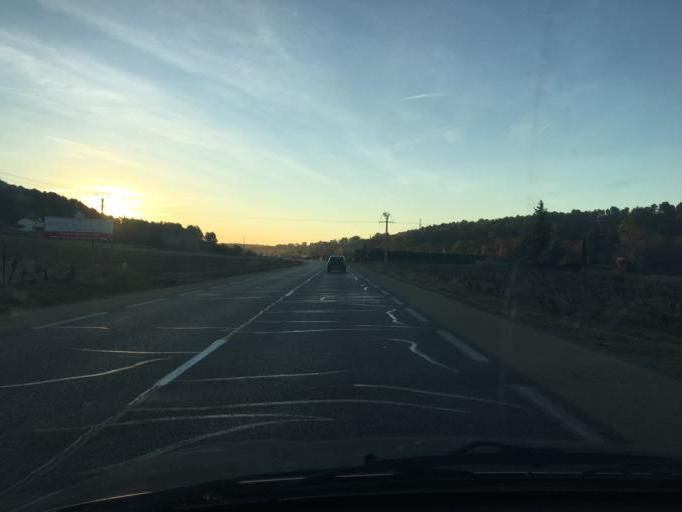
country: FR
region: Provence-Alpes-Cote d'Azur
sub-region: Departement du Var
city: Lorgues
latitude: 43.4764
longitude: 6.3744
